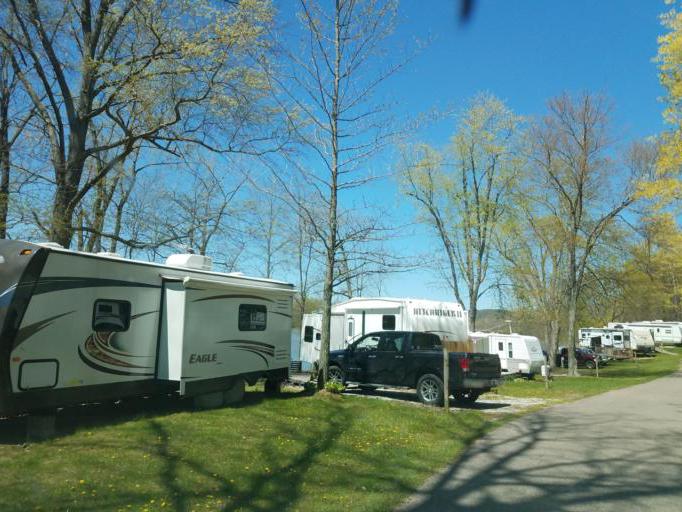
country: US
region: Ohio
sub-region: Richland County
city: Lincoln Heights
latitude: 40.7655
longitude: -82.3745
